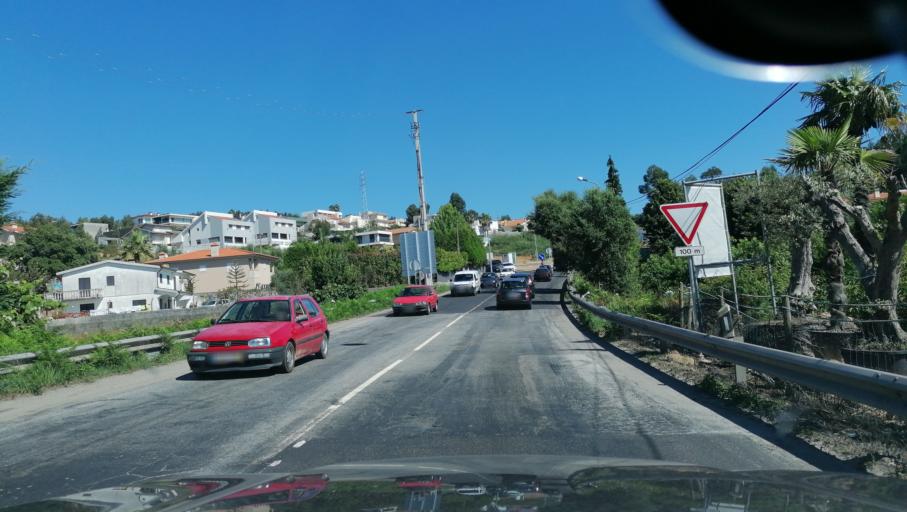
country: PT
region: Aveiro
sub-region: Santa Maria da Feira
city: Arrifana
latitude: 40.9300
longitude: -8.5129
